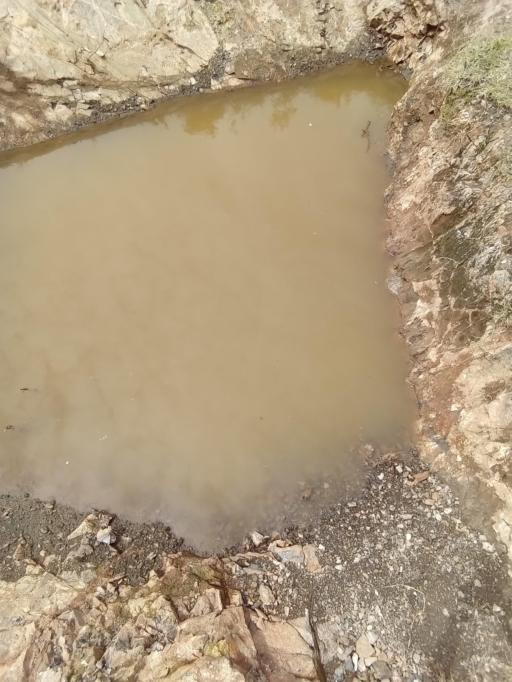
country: KE
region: Homa Bay
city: Homa Bay
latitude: -0.5112
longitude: 34.1661
